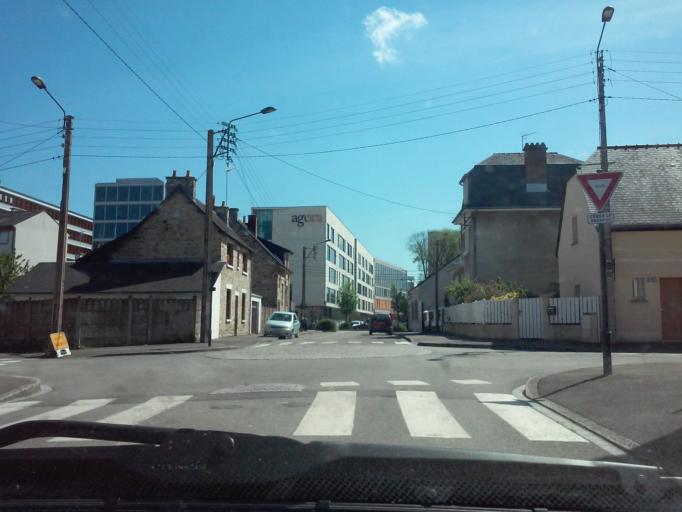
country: FR
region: Brittany
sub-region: Departement d'Ille-et-Vilaine
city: Rennes
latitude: 48.0948
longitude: -1.6759
